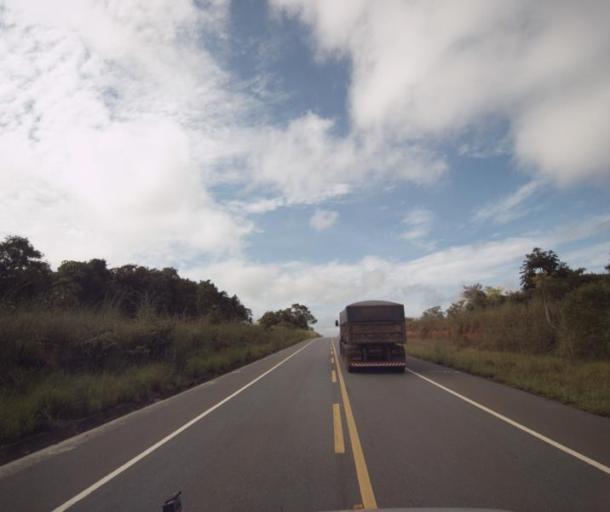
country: BR
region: Goias
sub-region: Barro Alto
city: Barro Alto
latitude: -15.2810
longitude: -48.6813
